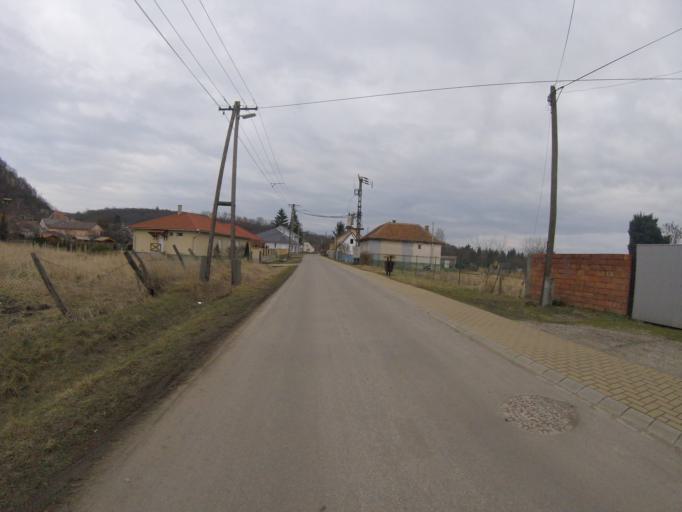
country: HU
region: Heves
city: Kerecsend
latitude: 47.8309
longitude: 20.3329
